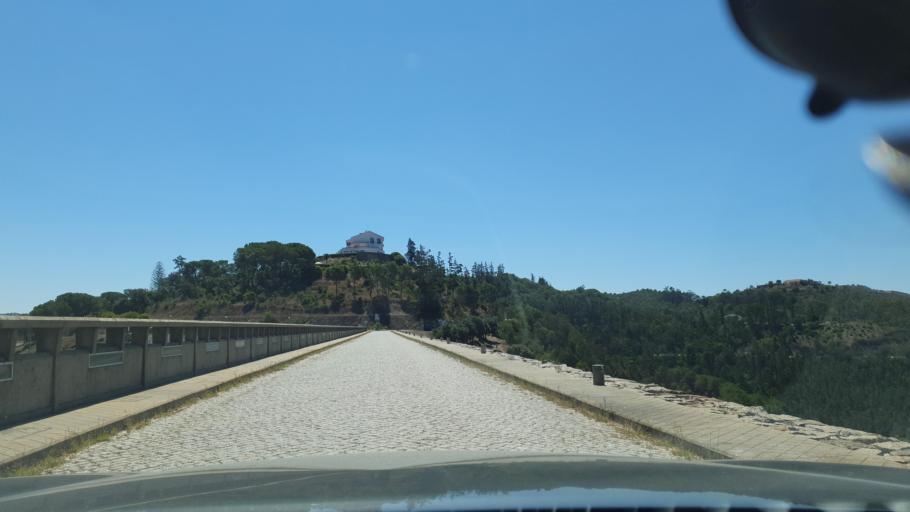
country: PT
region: Beja
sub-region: Odemira
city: Odemira
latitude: 37.5139
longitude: -8.4425
